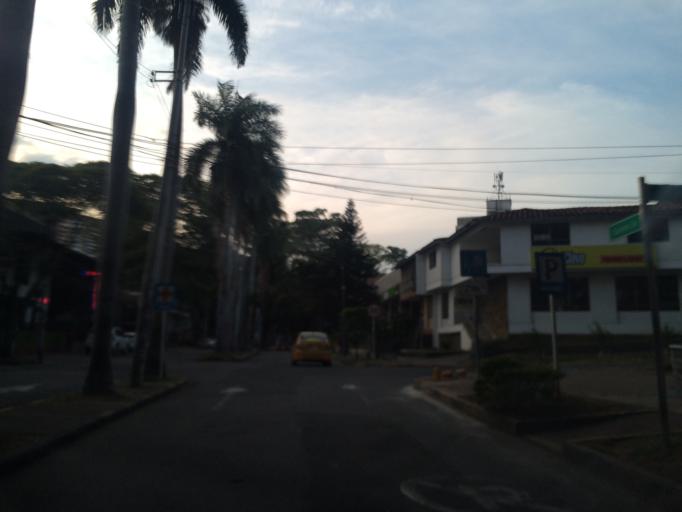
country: CO
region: Valle del Cauca
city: Cali
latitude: 3.4343
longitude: -76.5443
